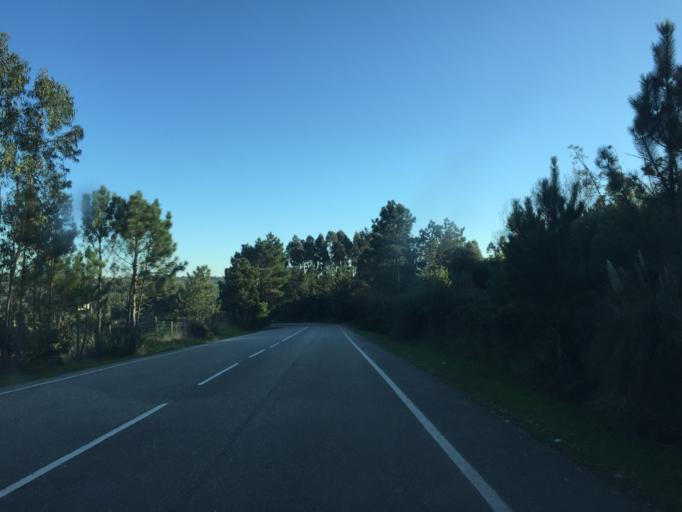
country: PT
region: Coimbra
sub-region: Figueira da Foz
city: Alhadas
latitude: 40.1563
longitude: -8.7987
